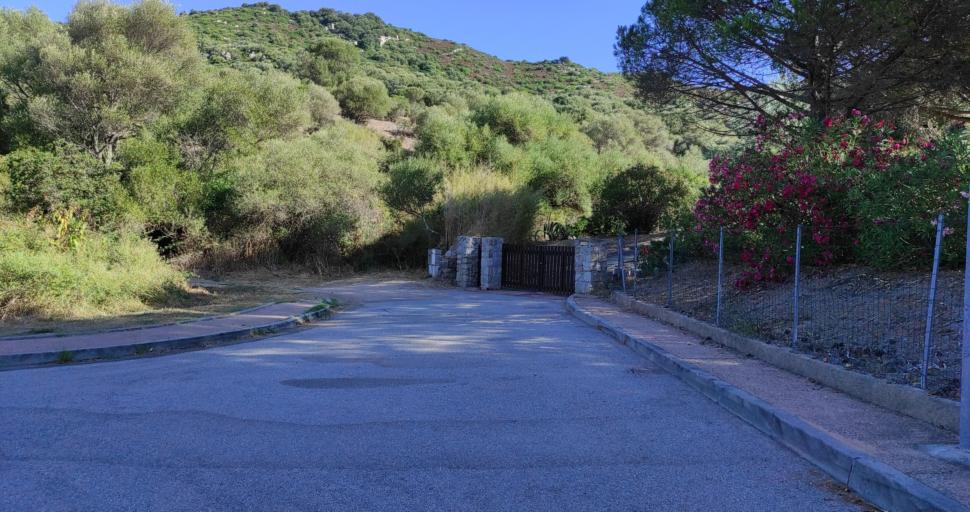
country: FR
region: Corsica
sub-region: Departement de la Corse-du-Sud
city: Alata
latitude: 41.9948
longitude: 8.6674
